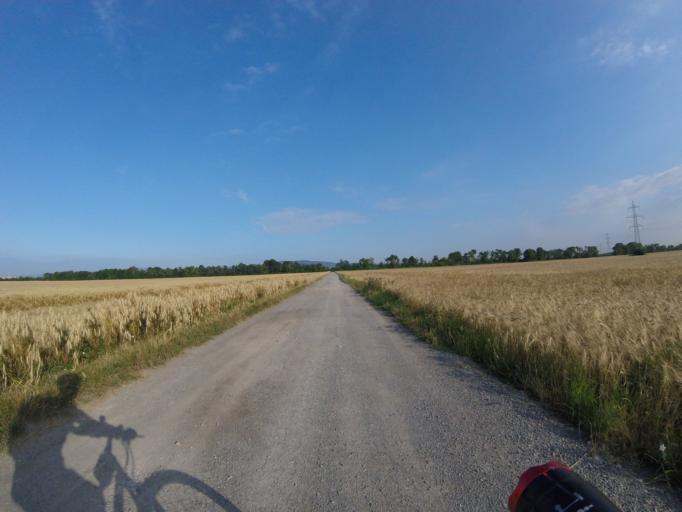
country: AT
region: Lower Austria
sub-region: Politischer Bezirk Baden
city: Trumau
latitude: 48.0002
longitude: 16.3723
